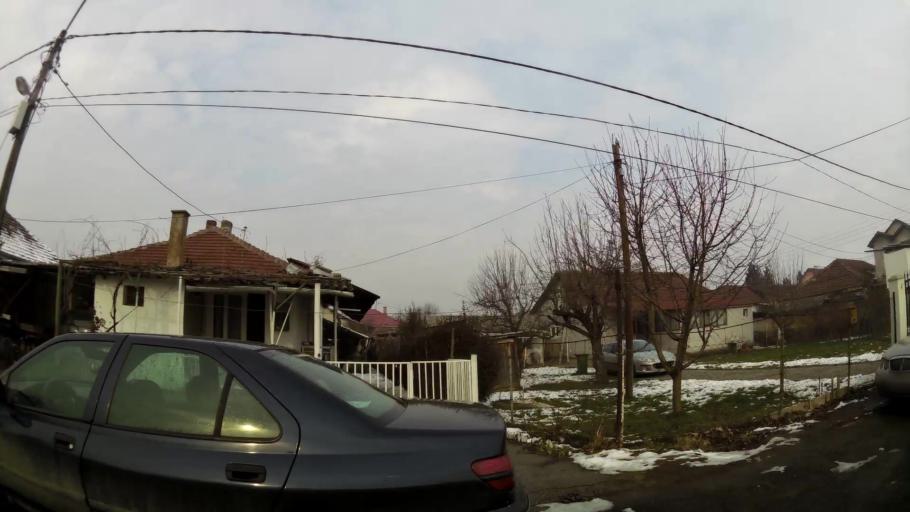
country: MK
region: Ilinden
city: Jurumleri
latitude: 41.9781
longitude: 21.5301
